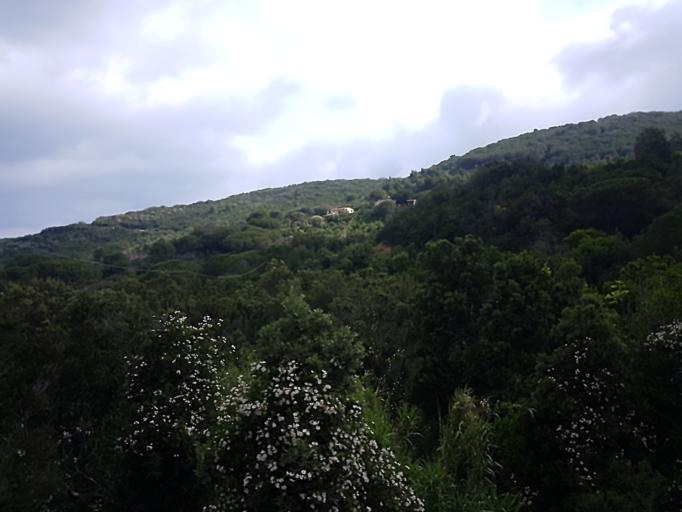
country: IT
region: Tuscany
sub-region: Provincia di Livorno
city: Campo nell'Elba
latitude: 42.7865
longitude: 10.2593
